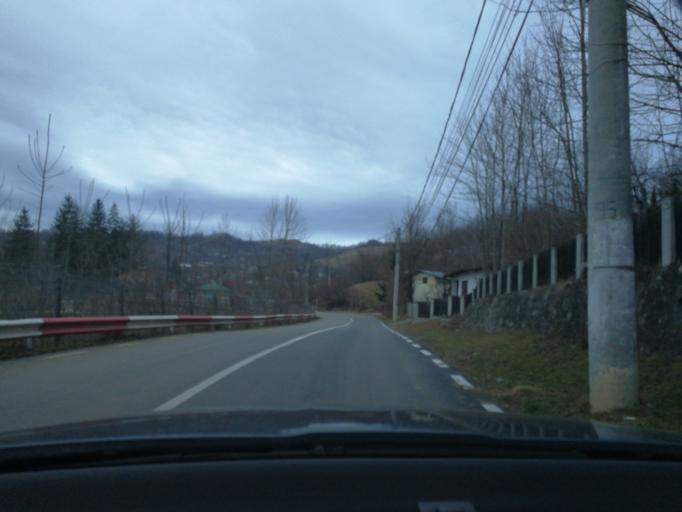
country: RO
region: Prahova
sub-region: Oras Breaza
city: Valea Tarsei
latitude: 45.1808
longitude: 25.6353
